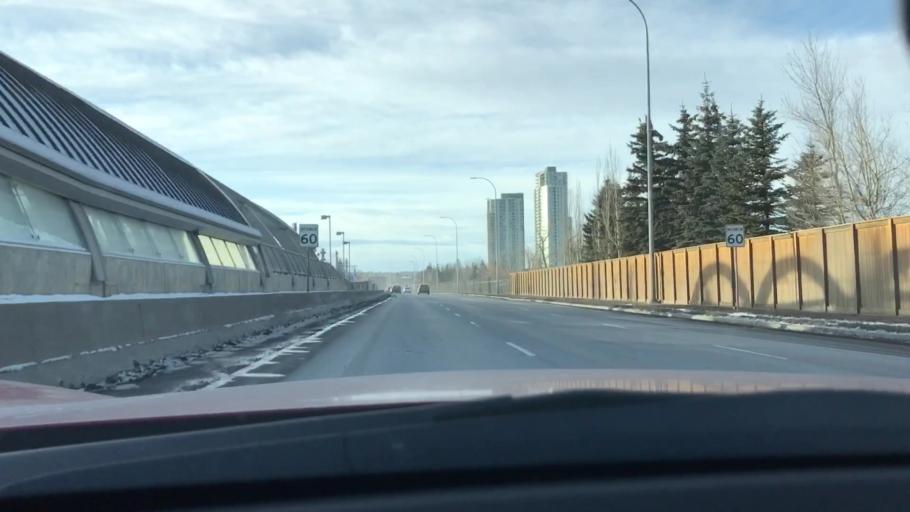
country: CA
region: Alberta
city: Calgary
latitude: 51.0418
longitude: -114.1253
